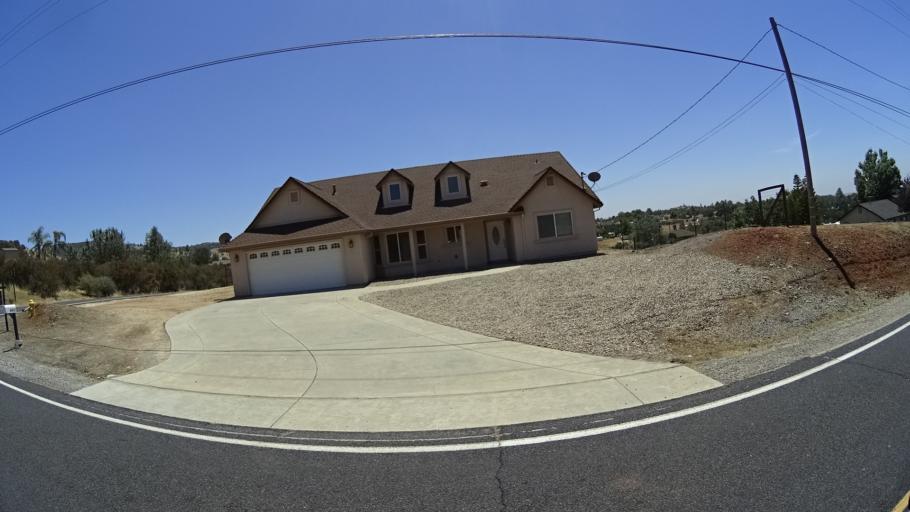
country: US
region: California
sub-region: Calaveras County
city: Rancho Calaveras
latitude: 38.1230
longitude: -120.8510
